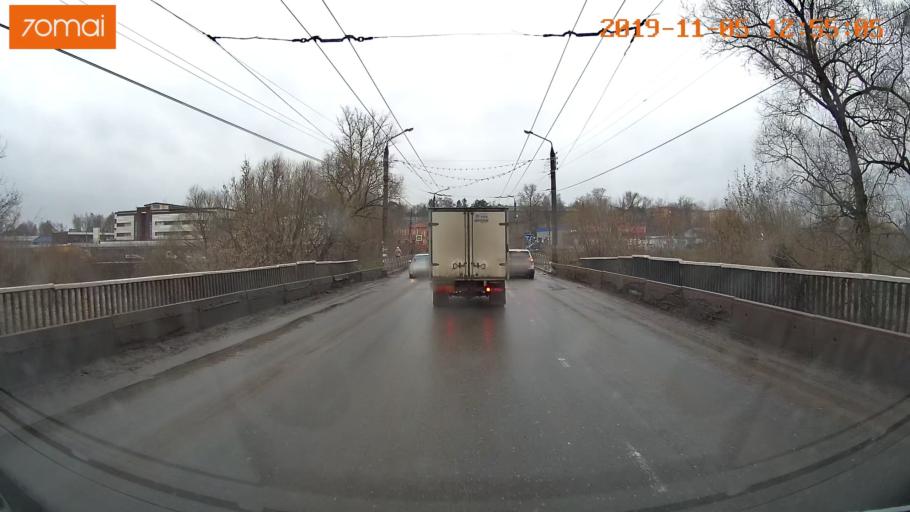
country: RU
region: Ivanovo
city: Kokhma
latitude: 56.9294
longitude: 41.0905
